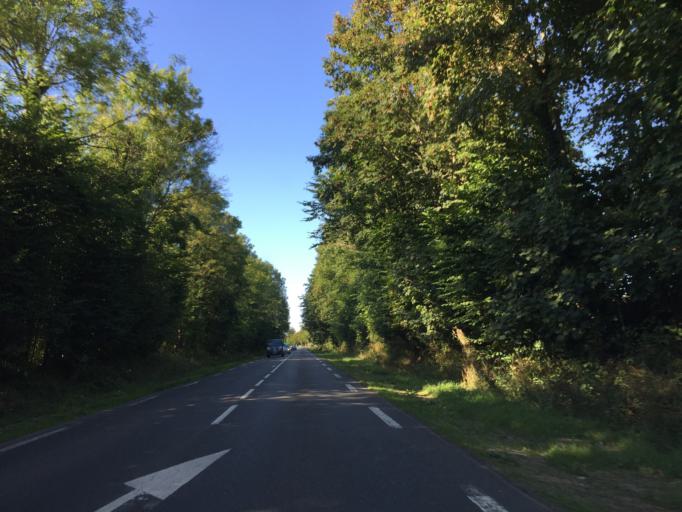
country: FR
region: Lower Normandy
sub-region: Departement du Calvados
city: Equemauville
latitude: 49.3724
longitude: 0.2056
